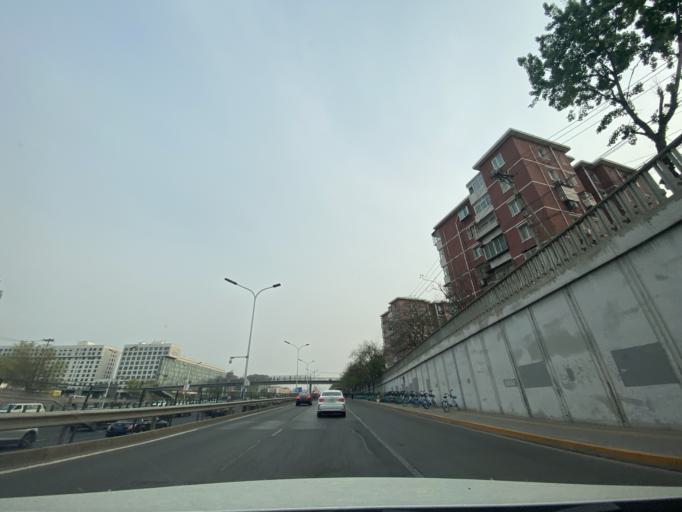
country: CN
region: Beijing
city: Sijiqing
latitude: 39.9329
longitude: 116.2683
